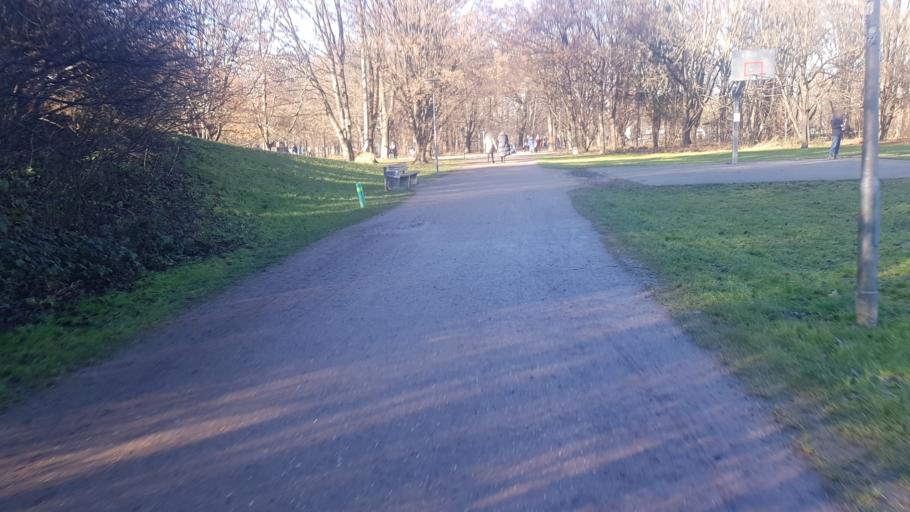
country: DE
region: Bavaria
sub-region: Upper Bavaria
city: Pasing
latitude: 48.1476
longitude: 11.5146
